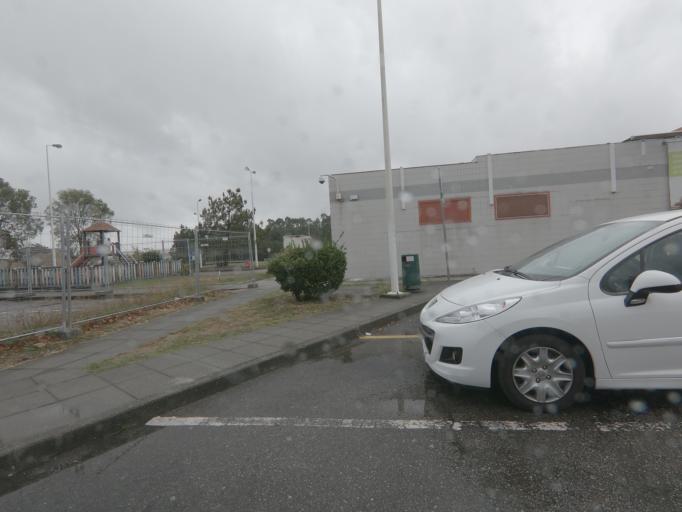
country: PT
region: Porto
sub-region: Maia
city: Pedroucos
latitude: 41.2000
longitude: -8.5662
